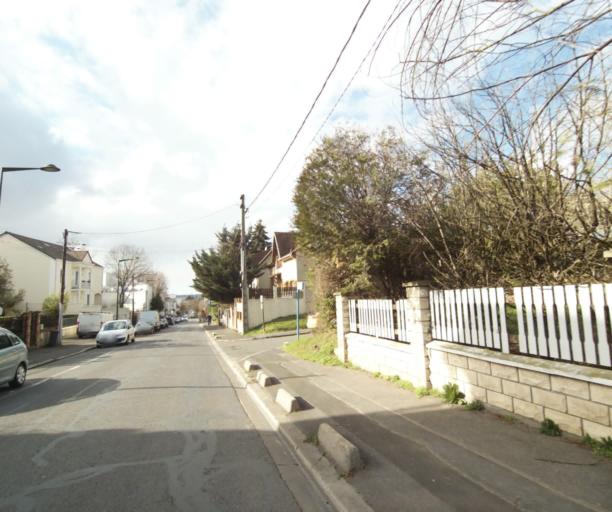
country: FR
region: Ile-de-France
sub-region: Departement de Seine-Saint-Denis
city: Villetaneuse
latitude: 48.9643
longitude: 2.3466
